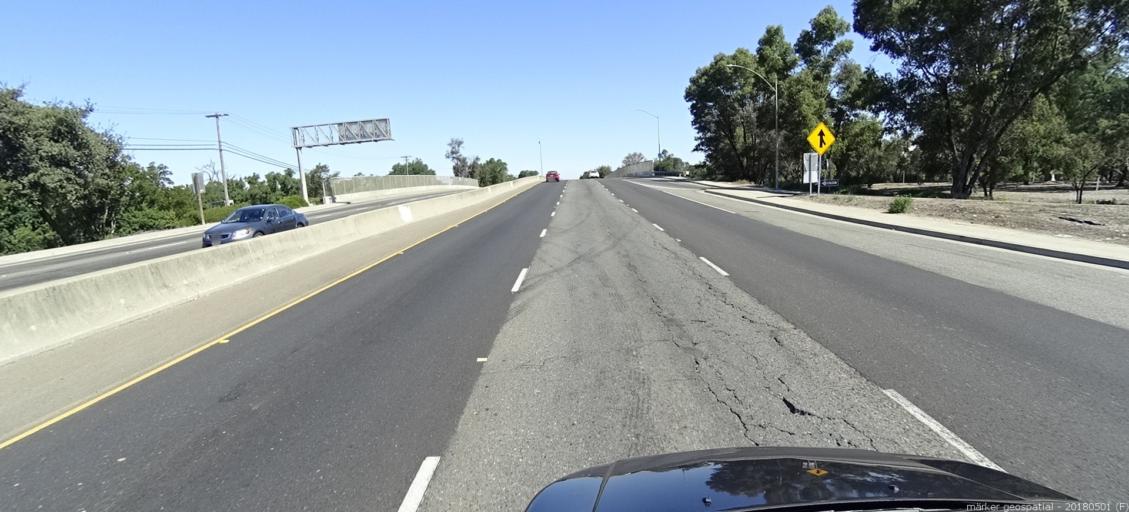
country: US
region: California
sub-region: Sacramento County
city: Arden-Arcade
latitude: 38.6386
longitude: -121.3830
